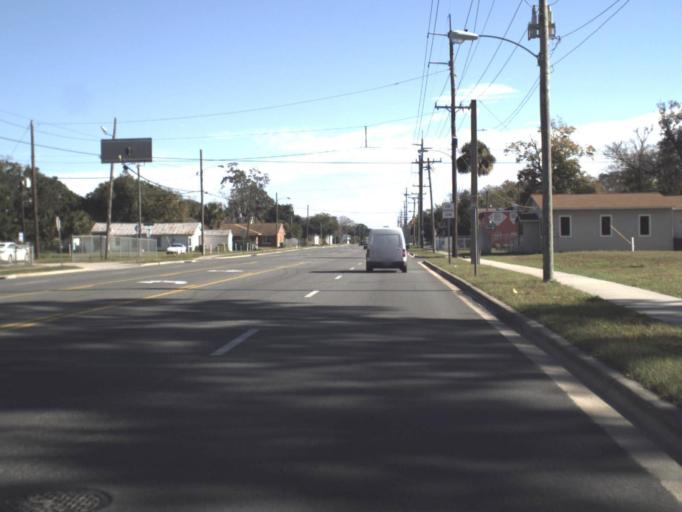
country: US
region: Florida
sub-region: Volusia County
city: Daytona Beach
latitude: 29.2128
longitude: -81.0393
